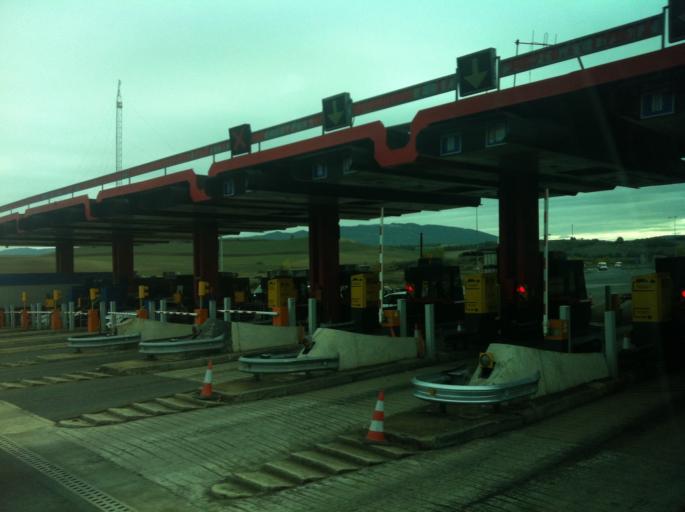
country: ES
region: Basque Country
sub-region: Provincia de Alava
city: Arminon
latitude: 42.7179
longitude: -2.8677
